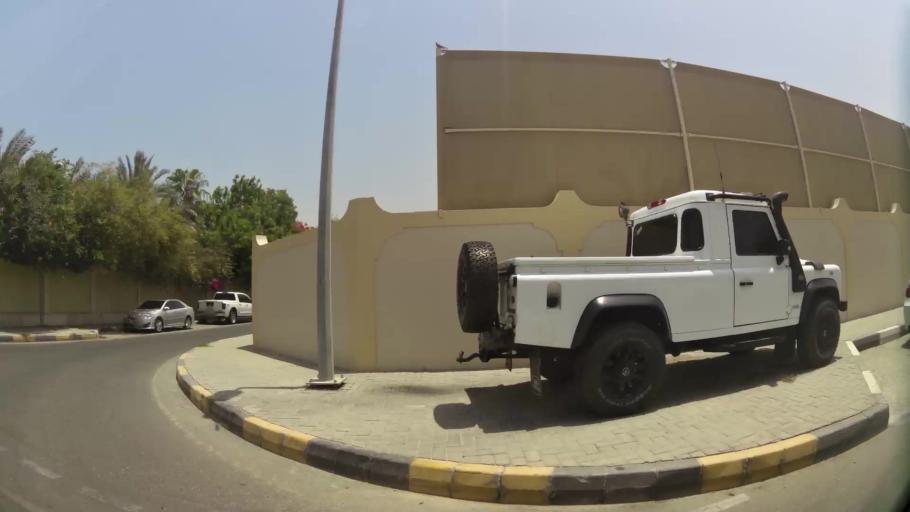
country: AE
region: Ash Shariqah
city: Sharjah
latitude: 25.3423
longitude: 55.3689
